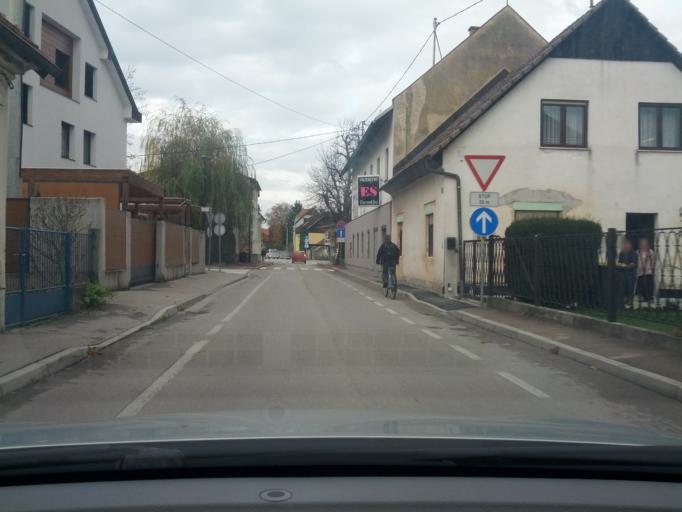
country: SI
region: Ljubljana
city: Ljubljana
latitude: 46.0468
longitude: 14.4848
